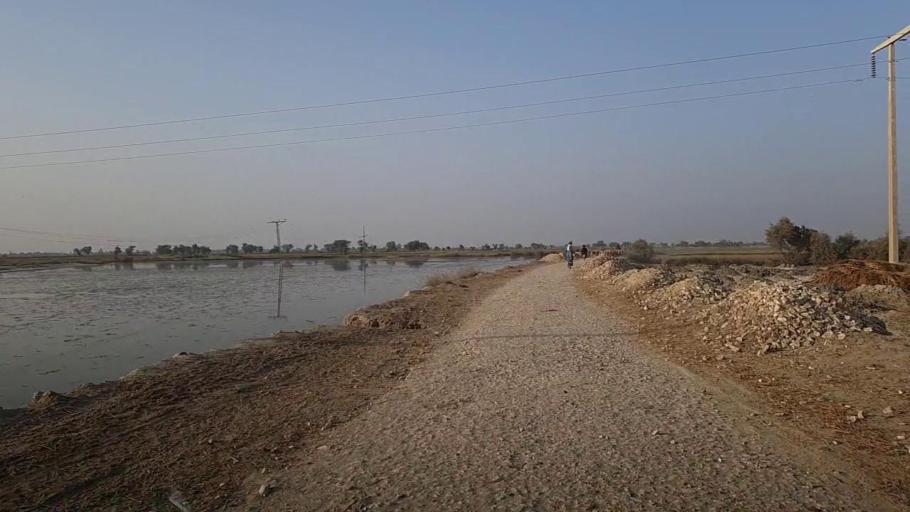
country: PK
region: Sindh
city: Tangwani
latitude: 28.2464
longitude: 69.0691
